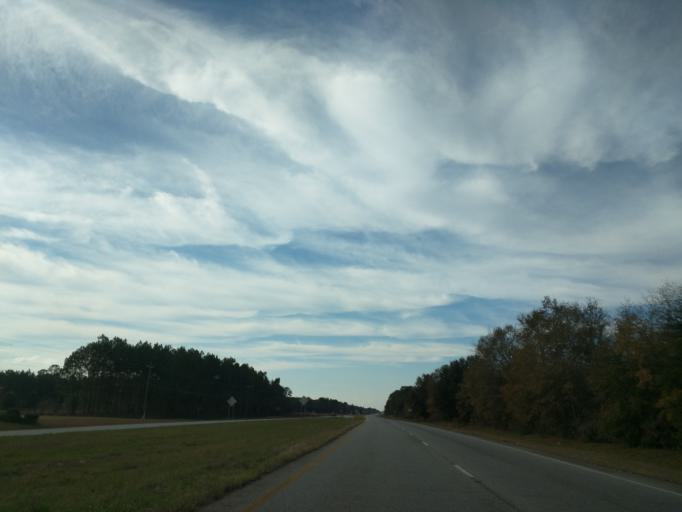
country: US
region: Georgia
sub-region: Decatur County
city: Bainbridge
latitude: 30.8882
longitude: -84.4797
